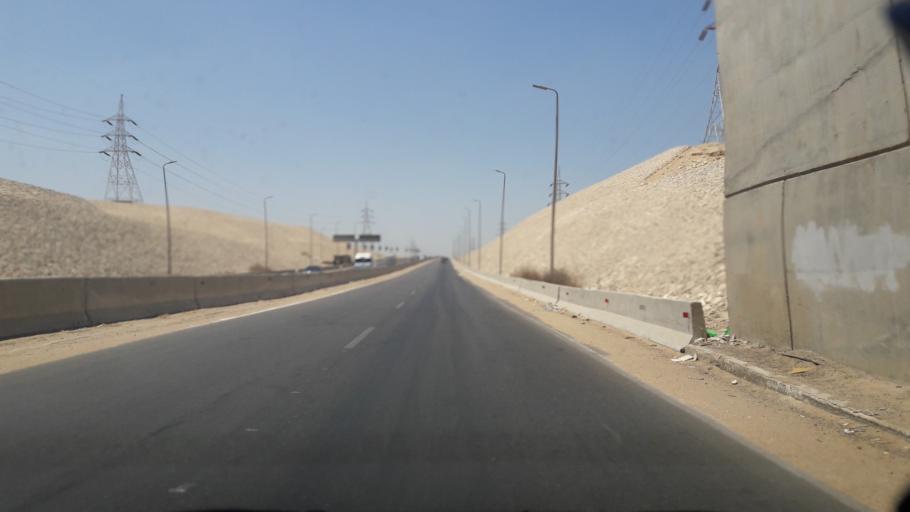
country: EG
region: Al Jizah
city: Al Jizah
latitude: 29.9992
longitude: 31.0910
